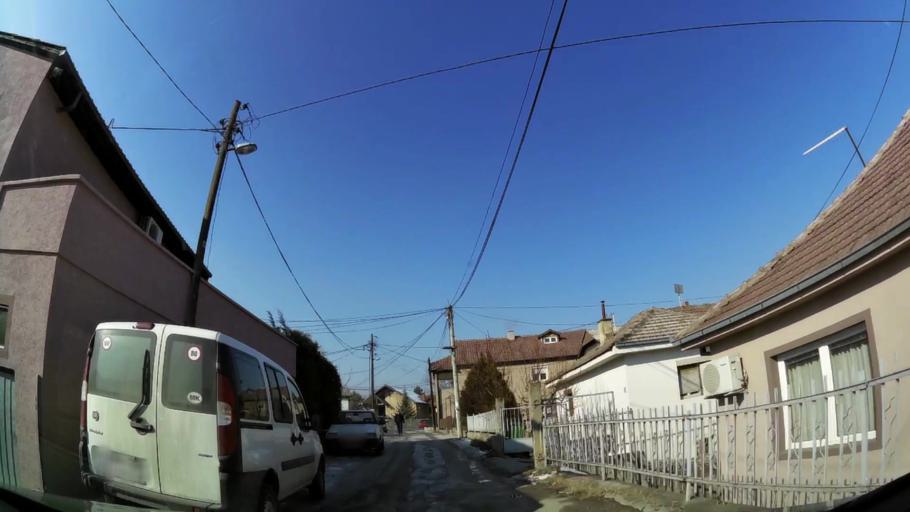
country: MK
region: Kisela Voda
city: Usje
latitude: 41.9708
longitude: 21.4520
